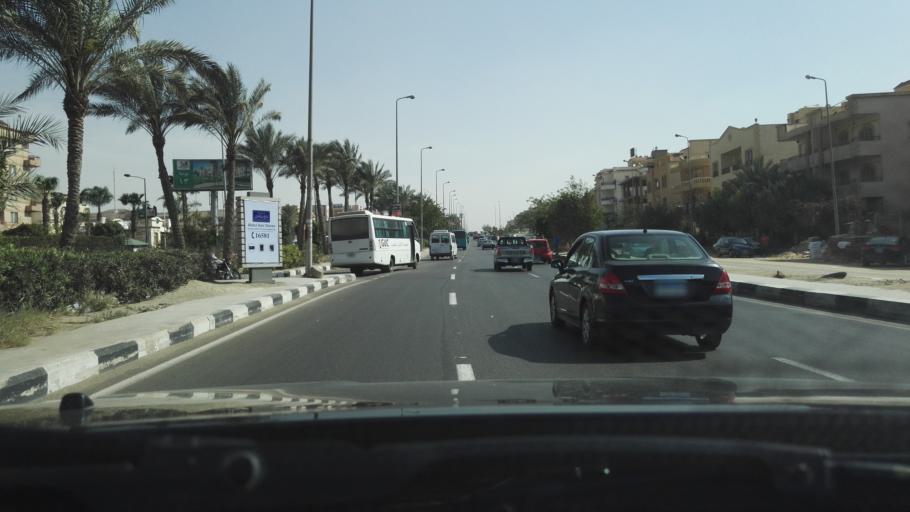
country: EG
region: Muhafazat al Qalyubiyah
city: Al Khankah
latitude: 30.0669
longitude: 31.4750
